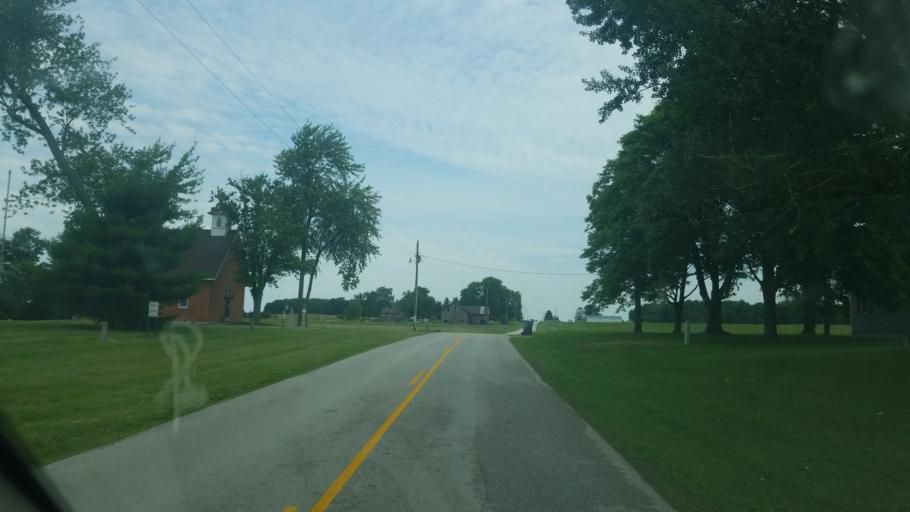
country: US
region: Ohio
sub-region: Wyandot County
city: Carey
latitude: 41.0351
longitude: -83.4399
